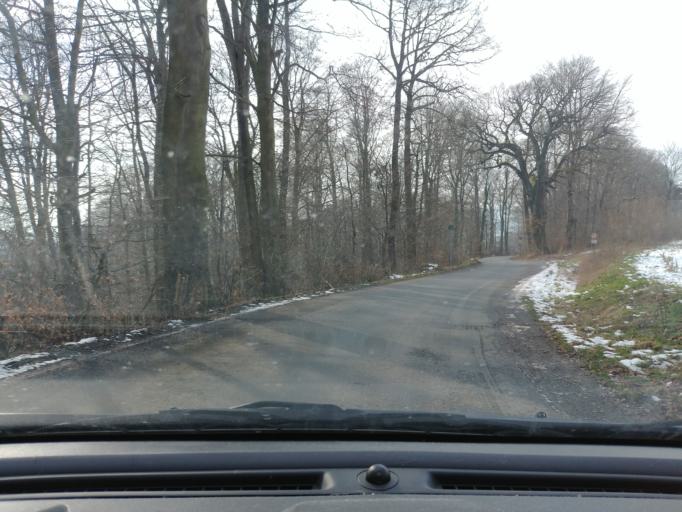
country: DE
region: Lower Saxony
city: Bad Karlshafen
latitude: 51.6521
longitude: 9.4376
